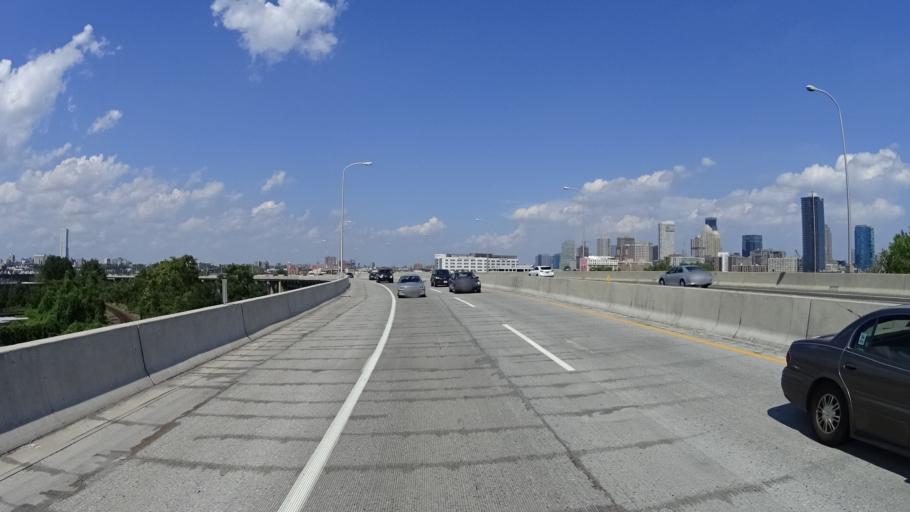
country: US
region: New Jersey
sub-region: Hudson County
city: Jersey City
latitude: 40.7104
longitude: -74.0550
